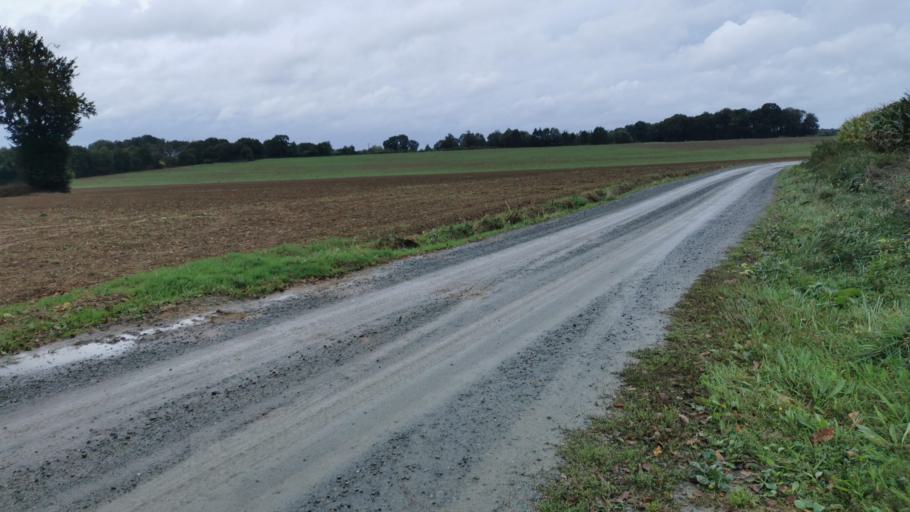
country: FR
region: Brittany
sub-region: Departement des Cotes-d'Armor
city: Pleslin-Trigavou
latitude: 48.5250
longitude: -2.0428
